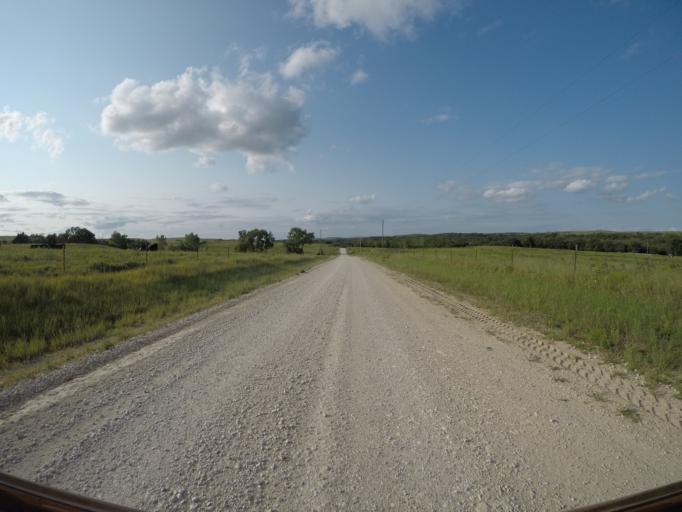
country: US
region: Kansas
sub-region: Wabaunsee County
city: Alma
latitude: 38.8736
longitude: -96.2059
